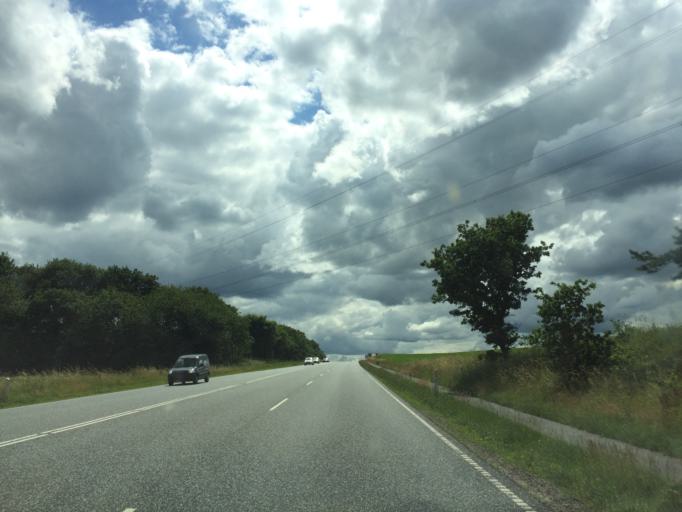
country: DK
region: Central Jutland
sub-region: Viborg Kommune
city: Viborg
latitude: 56.5490
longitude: 9.4788
